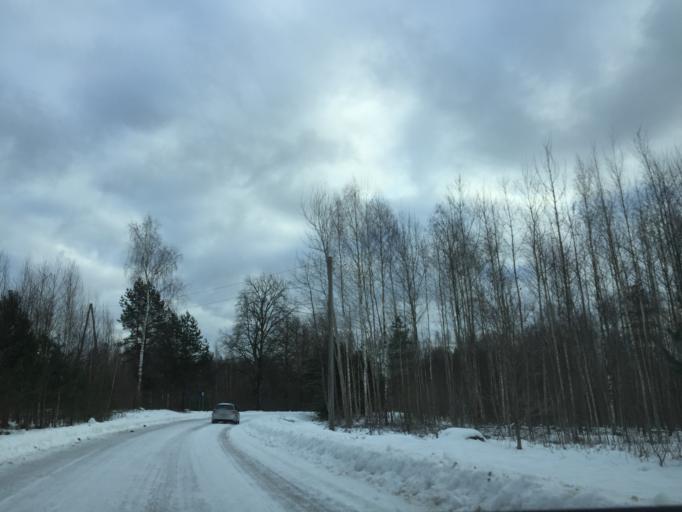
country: LV
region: Lielvarde
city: Lielvarde
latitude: 56.5802
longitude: 24.7856
